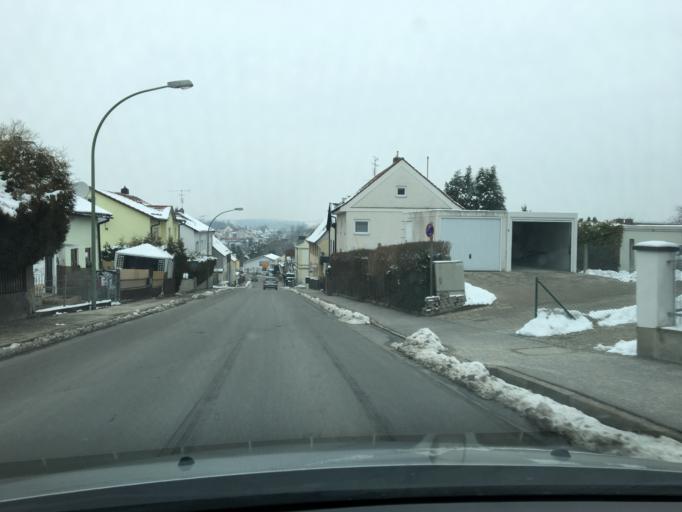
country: DE
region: Bavaria
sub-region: Lower Bavaria
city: Vilsbiburg
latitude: 48.4456
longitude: 12.3620
